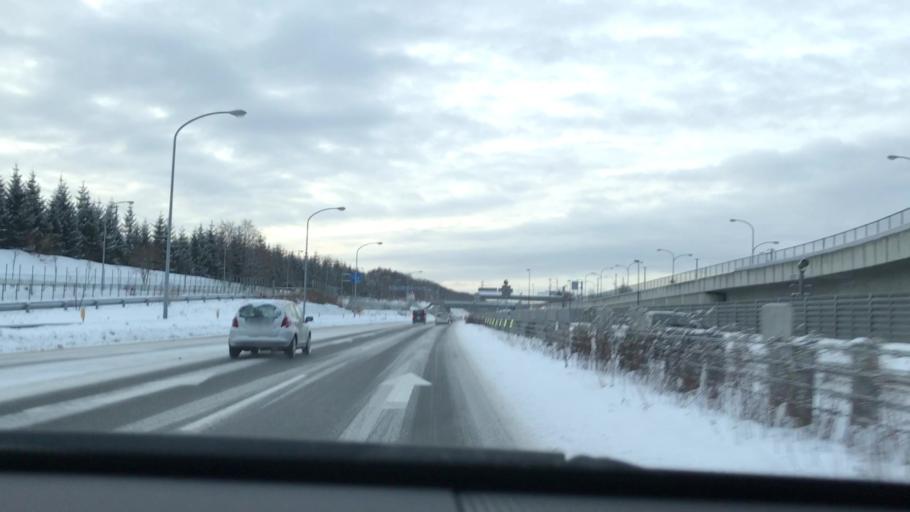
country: JP
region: Hokkaido
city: Kitahiroshima
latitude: 43.0130
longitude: 141.4651
